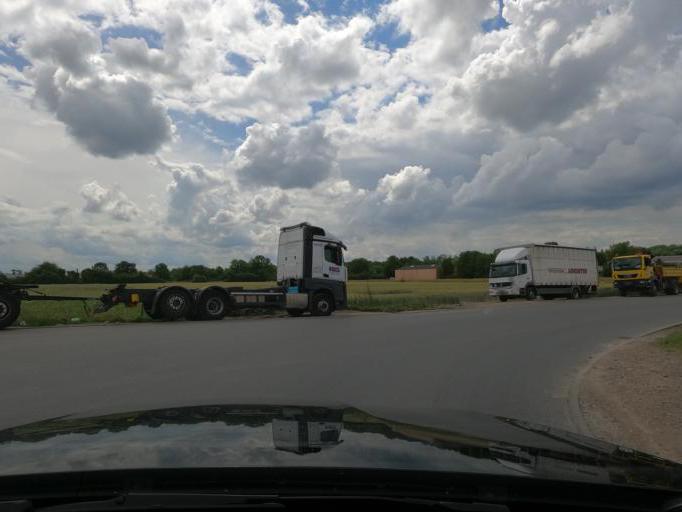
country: DE
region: Lower Saxony
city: Laatzen
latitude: 52.3640
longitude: 9.8732
